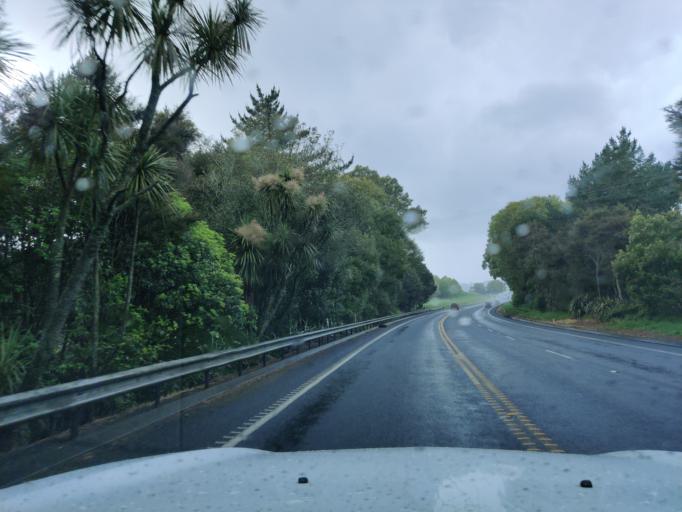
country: NZ
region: Waikato
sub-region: Waipa District
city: Cambridge
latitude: -37.9412
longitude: 175.5812
